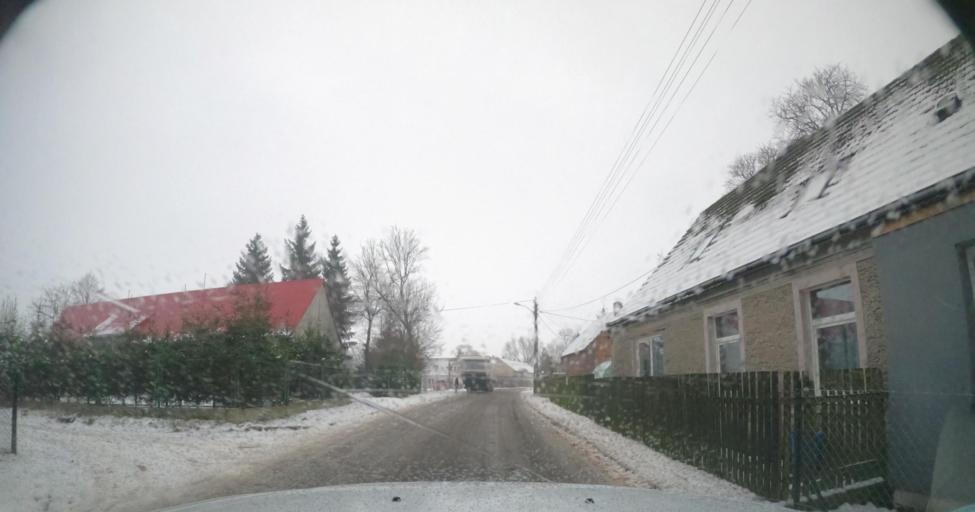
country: PL
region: West Pomeranian Voivodeship
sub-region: Powiat kamienski
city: Golczewo
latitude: 53.7669
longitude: 14.9092
